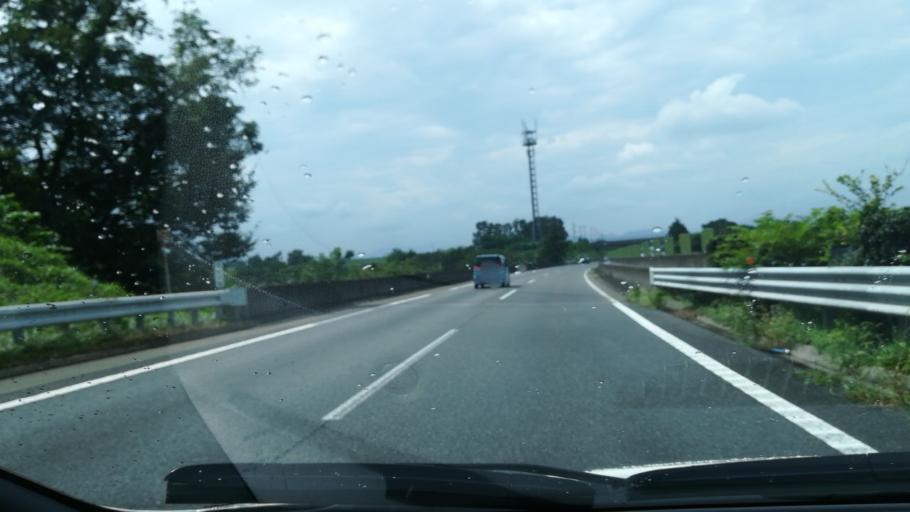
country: JP
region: Gunma
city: Tomioka
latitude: 36.2394
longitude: 138.9341
